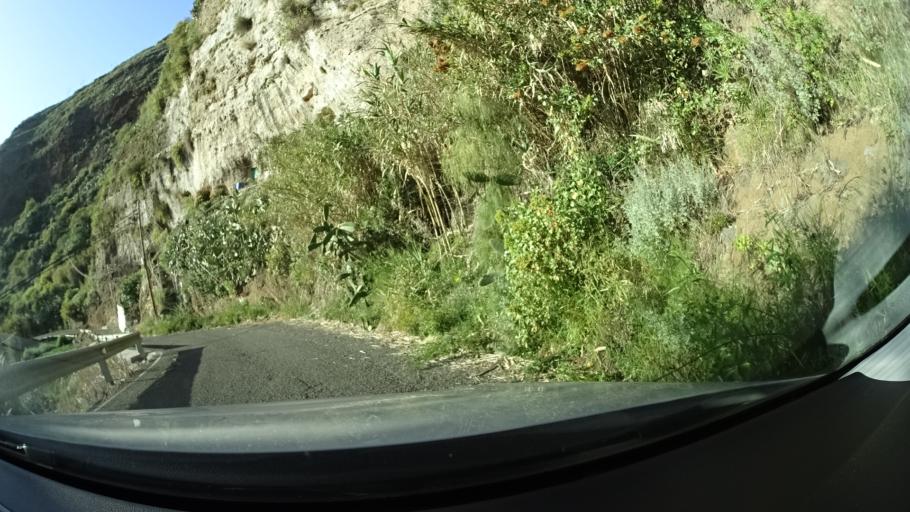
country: ES
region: Canary Islands
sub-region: Provincia de Las Palmas
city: Artenara
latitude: 28.0462
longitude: -15.6598
